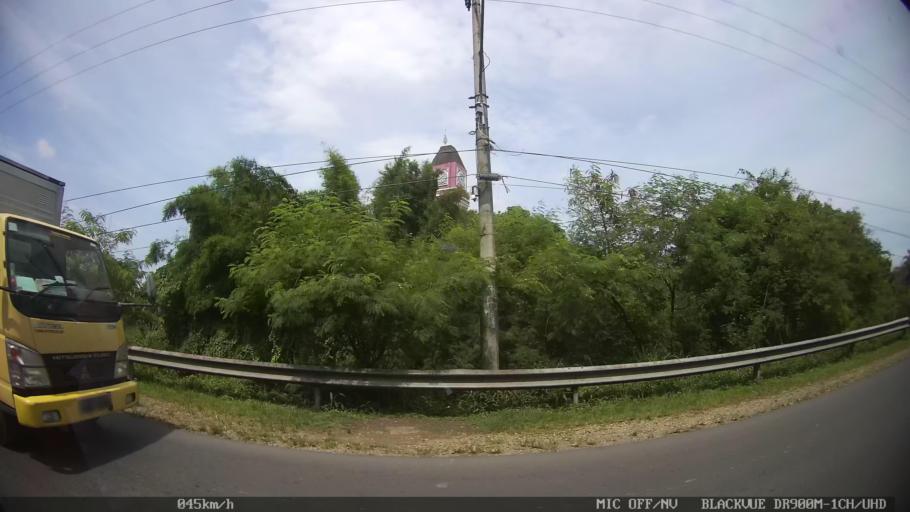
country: ID
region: North Sumatra
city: Medan
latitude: 3.6364
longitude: 98.7080
